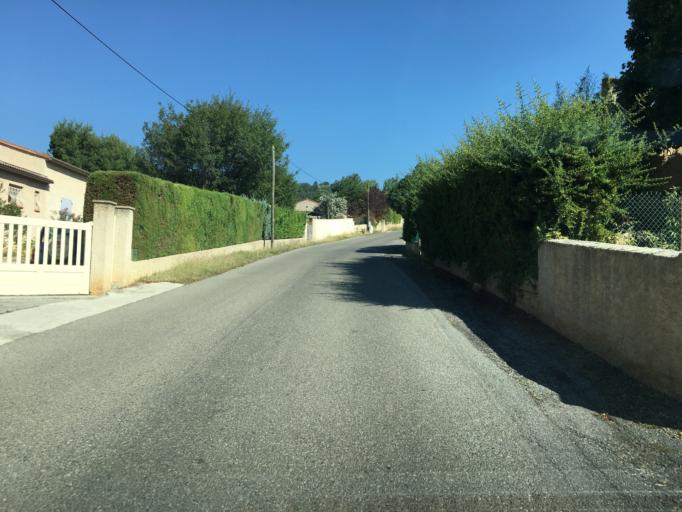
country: FR
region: Provence-Alpes-Cote d'Azur
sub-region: Departement des Alpes-de-Haute-Provence
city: Mallemoisson
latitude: 44.0527
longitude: 6.1325
